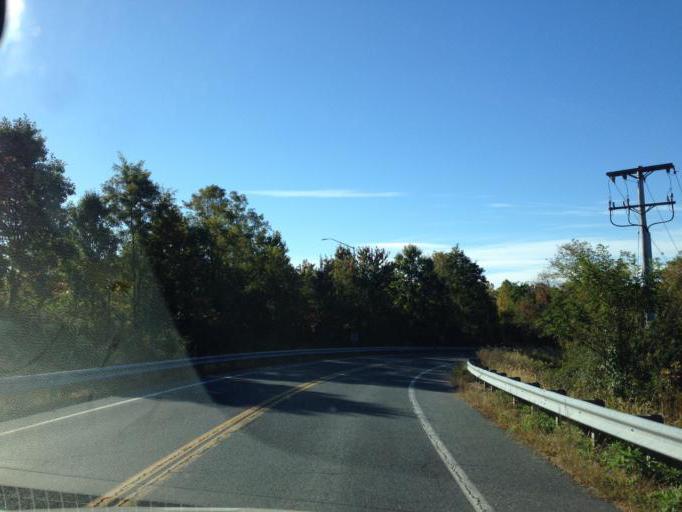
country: US
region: Maryland
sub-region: Howard County
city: Fulton
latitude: 39.1437
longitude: -76.9043
